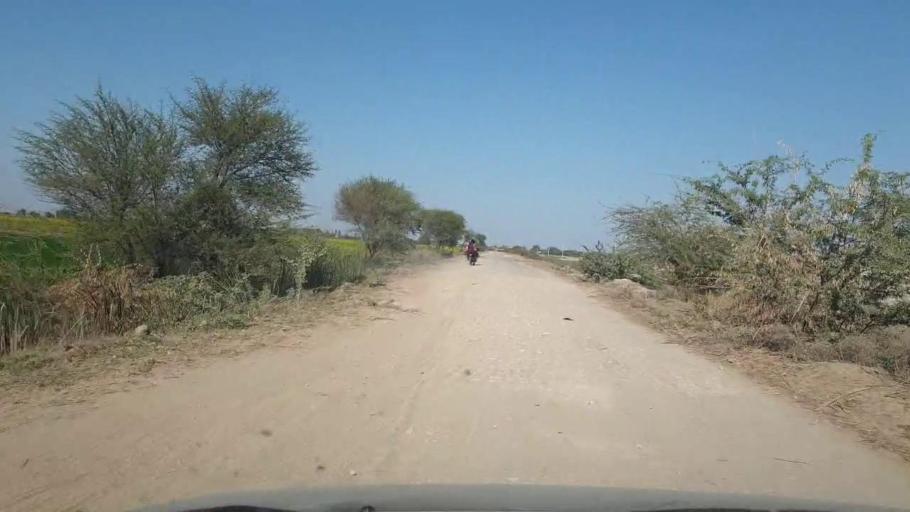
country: PK
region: Sindh
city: Samaro
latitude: 25.3557
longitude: 69.3165
